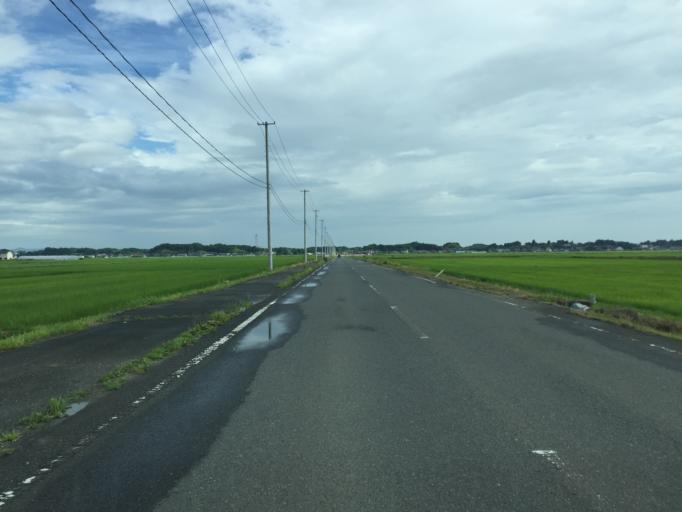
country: JP
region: Miyagi
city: Marumori
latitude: 37.7906
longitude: 140.9571
